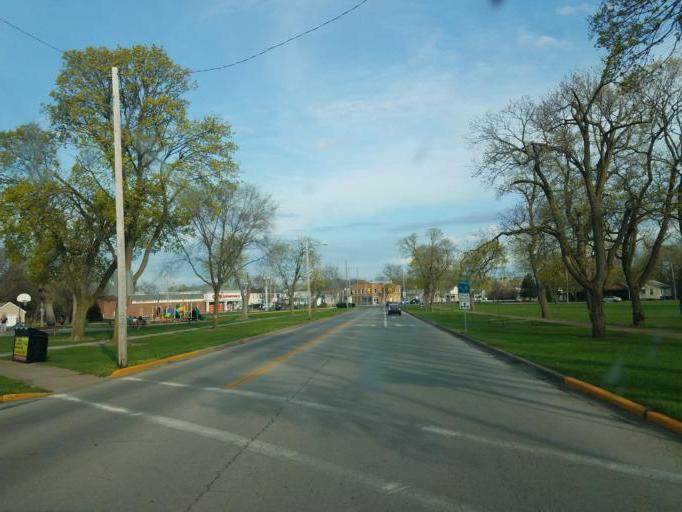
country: US
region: Ohio
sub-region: Erie County
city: Sandusky
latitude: 41.4531
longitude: -82.7039
